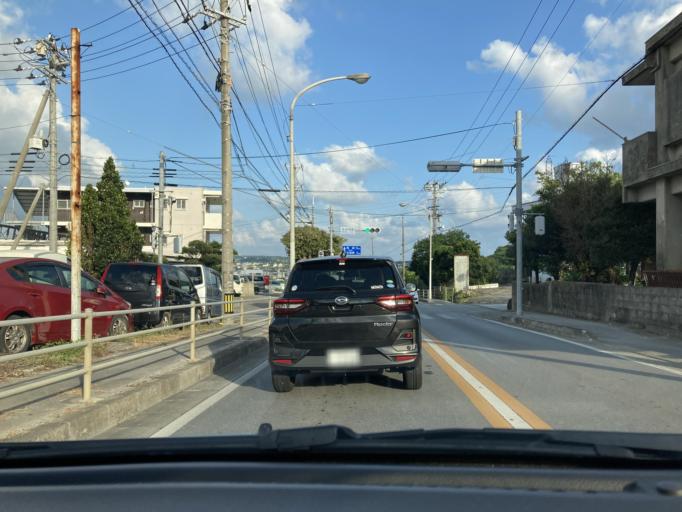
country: JP
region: Okinawa
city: Tomigusuku
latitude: 26.1500
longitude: 127.7108
